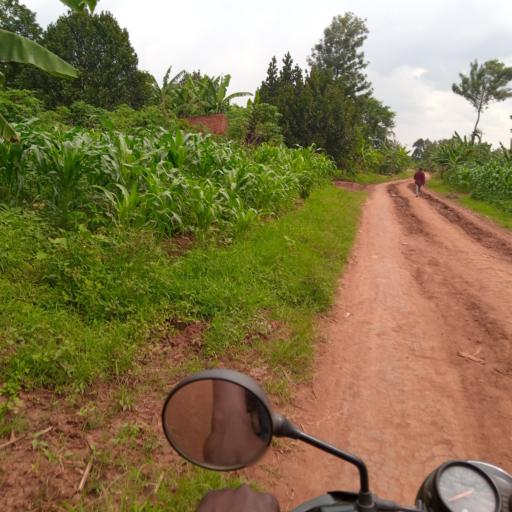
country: UG
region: Eastern Region
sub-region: Mbale District
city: Mbale
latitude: 1.1163
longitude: 34.1939
